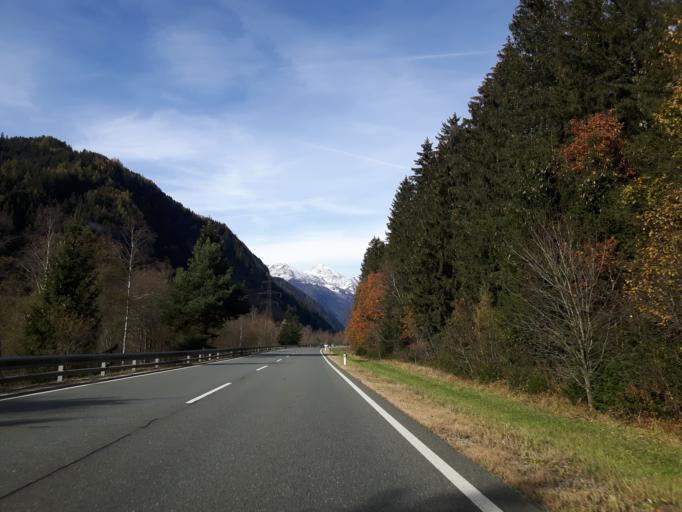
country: AT
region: Tyrol
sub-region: Politischer Bezirk Lienz
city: Schlaiten
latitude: 46.8862
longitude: 12.6567
